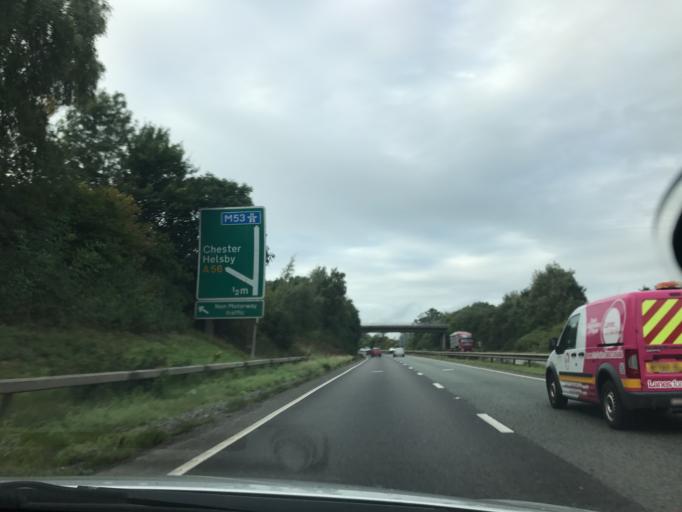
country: GB
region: England
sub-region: Cheshire West and Chester
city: Guilden Sutton
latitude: 53.2009
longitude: -2.8438
